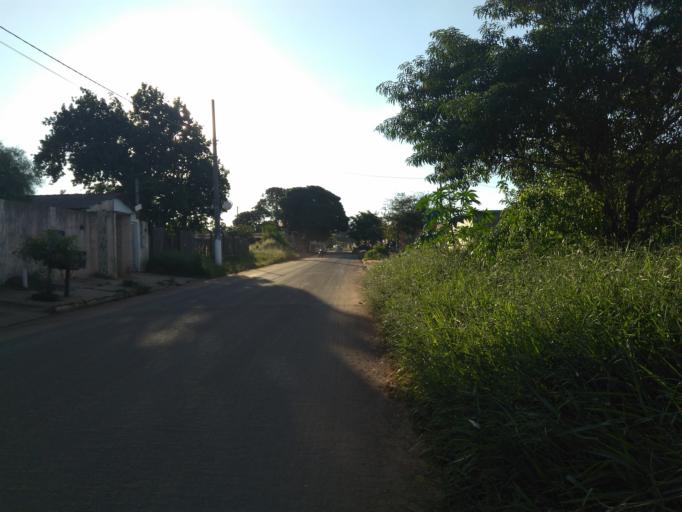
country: BR
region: Mato Grosso do Sul
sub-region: Ponta Pora
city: Ponta Pora
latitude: -22.5013
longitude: -55.7291
